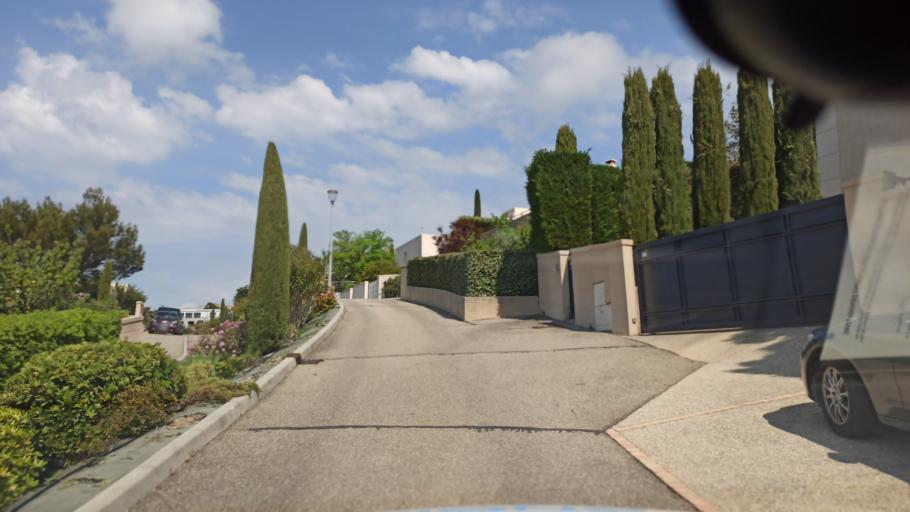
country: FR
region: Languedoc-Roussillon
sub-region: Departement du Gard
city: Les Angles
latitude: 43.9685
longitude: 4.7769
